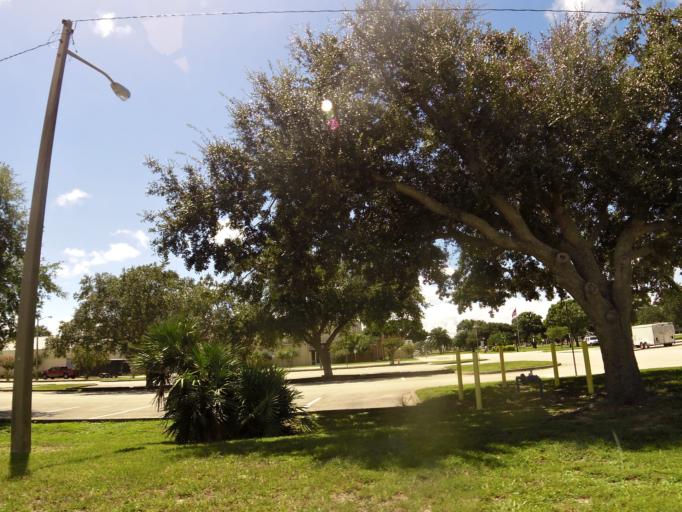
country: US
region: Florida
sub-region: Brevard County
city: Melbourne
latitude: 28.0841
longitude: -80.6101
